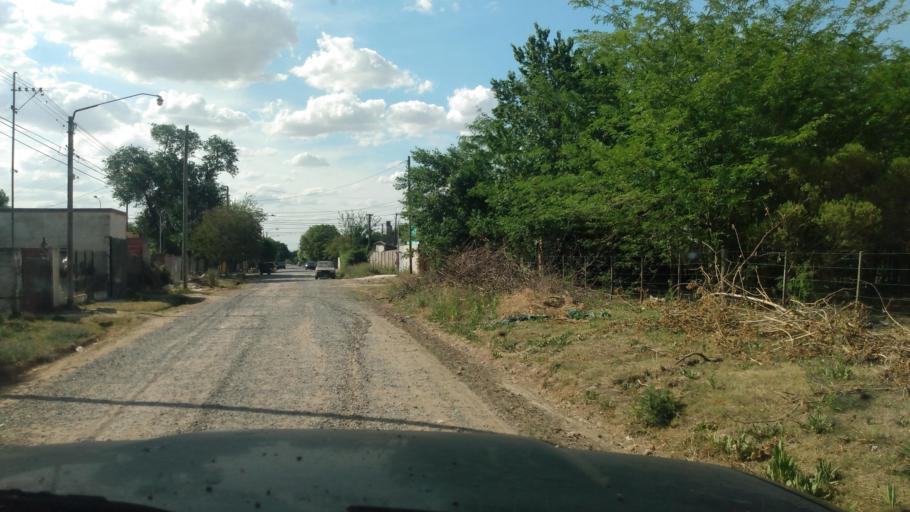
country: AR
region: Buenos Aires
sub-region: Partido de Lujan
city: Lujan
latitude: -34.5511
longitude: -59.1041
